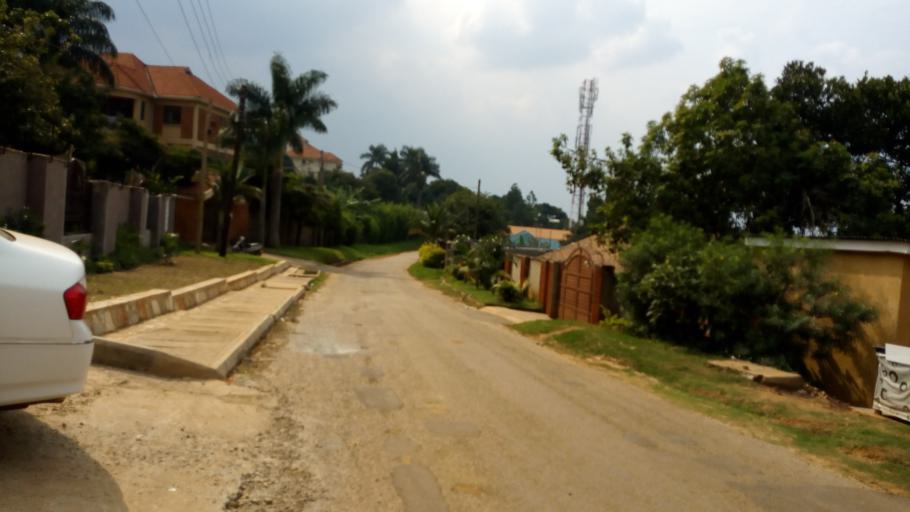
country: UG
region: Central Region
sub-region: Wakiso District
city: Kireka
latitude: 0.3119
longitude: 32.6467
